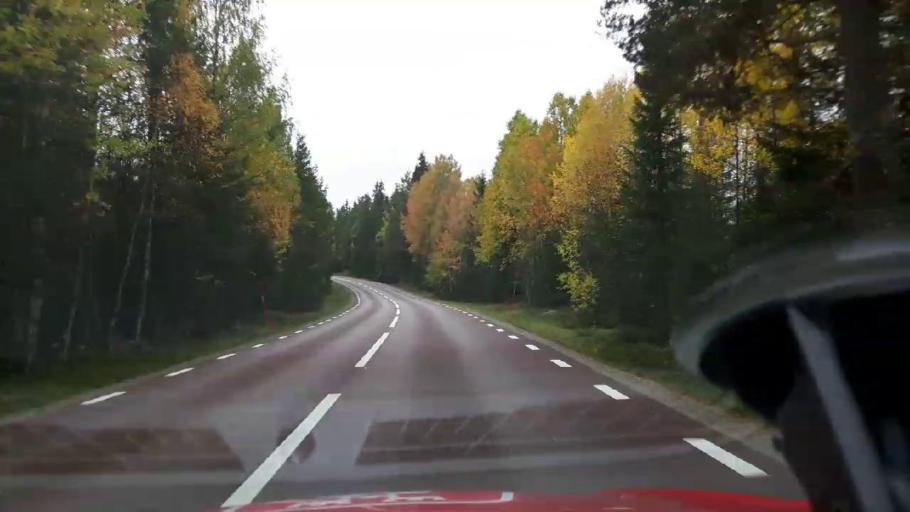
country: SE
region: Jaemtland
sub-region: Harjedalens Kommun
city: Sveg
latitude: 62.2143
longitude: 14.8451
